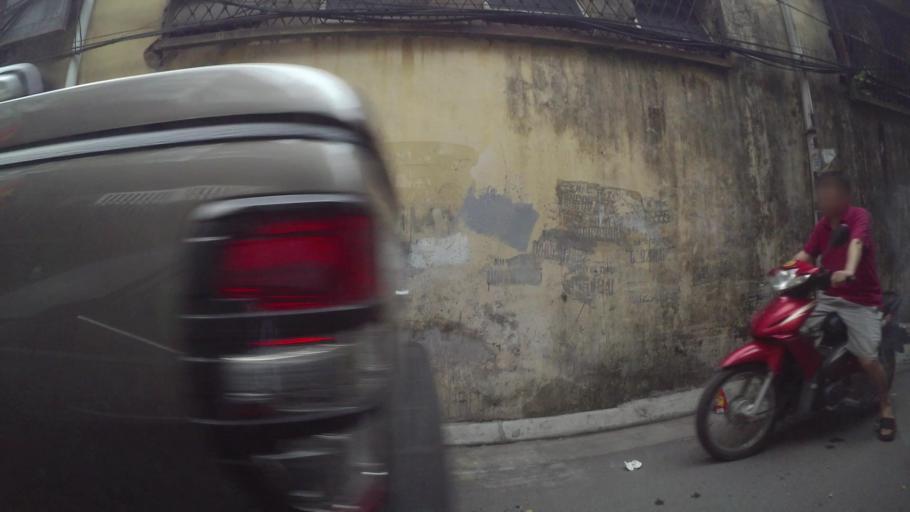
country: VN
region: Ha Noi
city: Hoan Kiem
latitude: 21.0579
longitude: 105.8955
